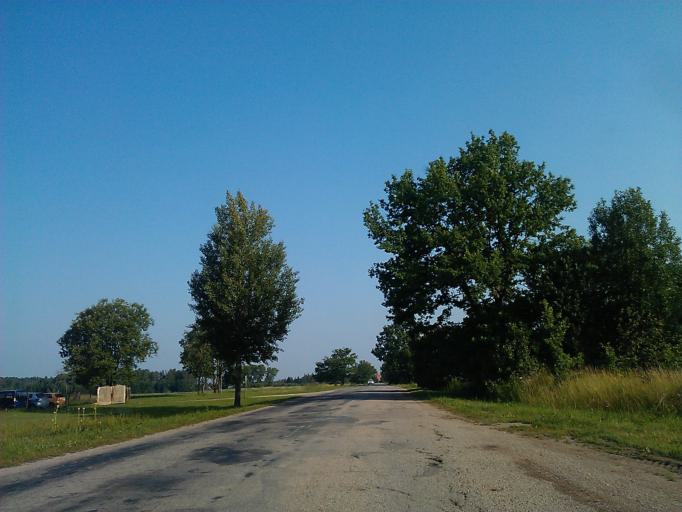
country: LV
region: Aizpute
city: Aizpute
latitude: 56.6986
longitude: 21.6307
